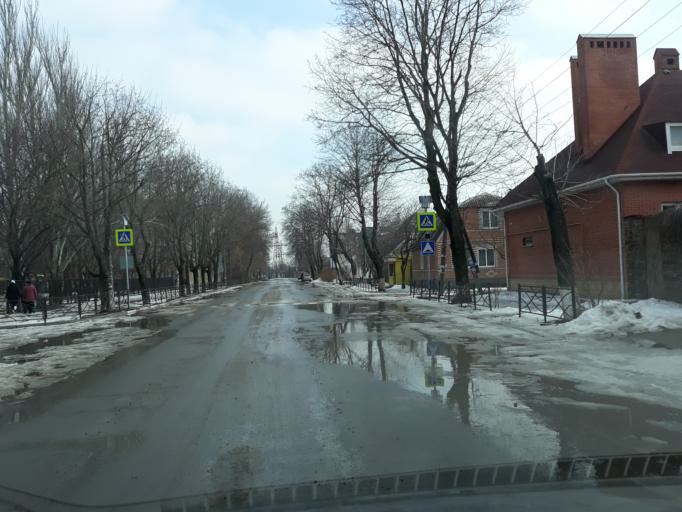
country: RU
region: Rostov
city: Taganrog
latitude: 47.2190
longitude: 38.8880
